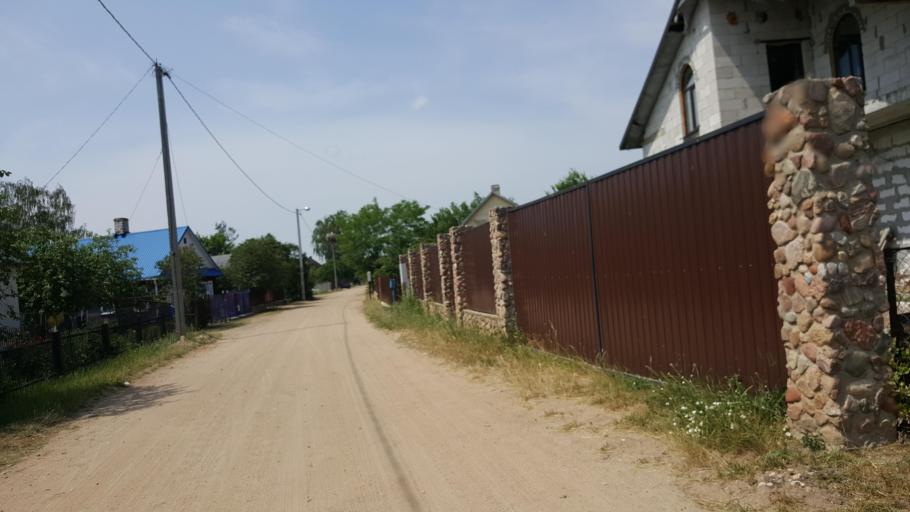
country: BY
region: Brest
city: Kamyanyets
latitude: 52.3735
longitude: 23.7802
